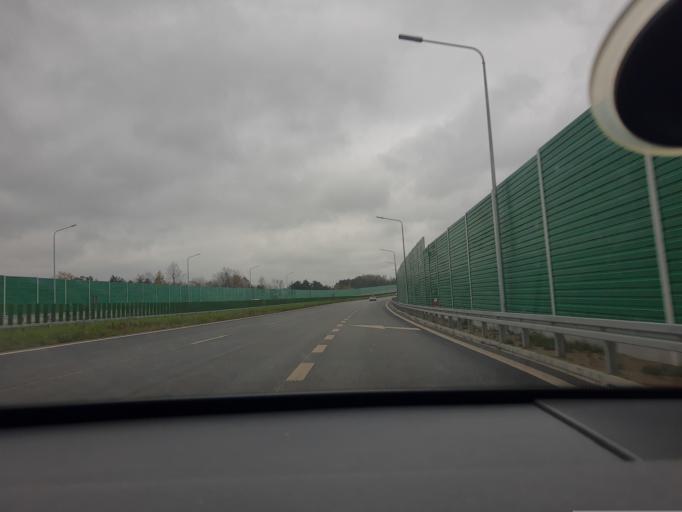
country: PL
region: Lodz Voivodeship
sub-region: Powiat pabianicki
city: Konstantynow Lodzki
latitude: 51.7271
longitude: 19.3561
